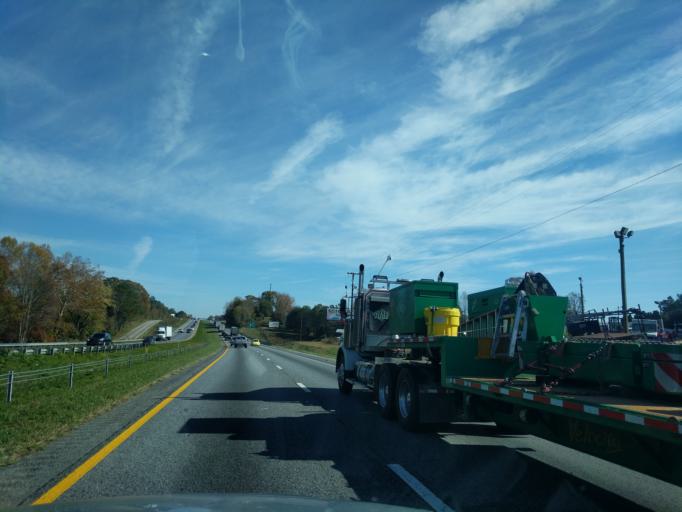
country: US
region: South Carolina
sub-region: Spartanburg County
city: Cowpens
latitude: 35.0365
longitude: -81.8353
